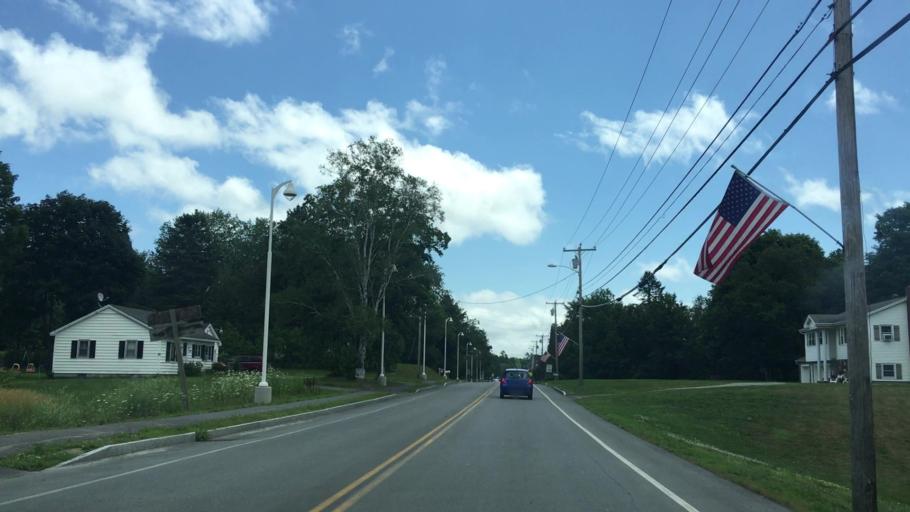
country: US
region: Maine
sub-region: Penobscot County
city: Hermon
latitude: 44.8081
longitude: -68.9072
